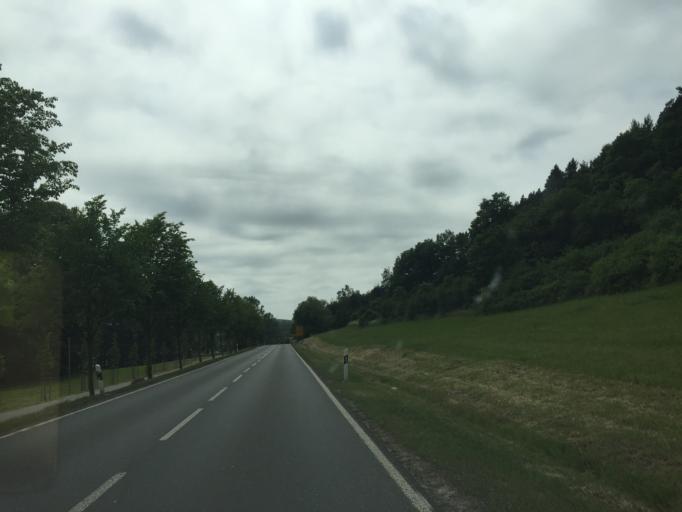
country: DE
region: Thuringia
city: Bechstedt
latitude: 50.6727
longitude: 11.1491
